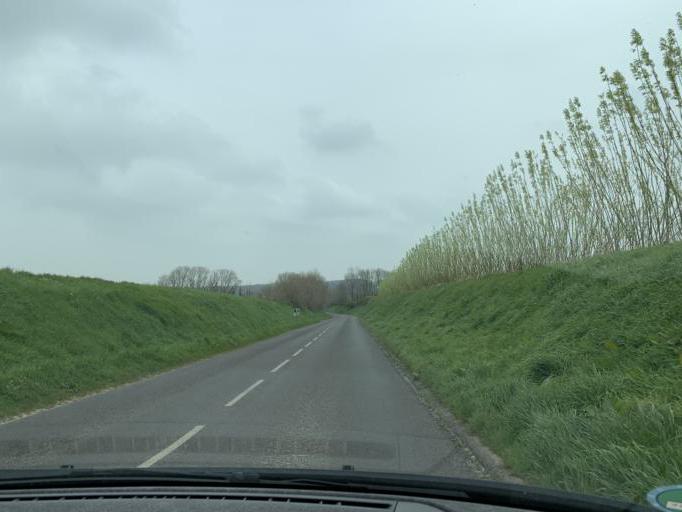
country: FR
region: Haute-Normandie
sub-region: Departement de la Seine-Maritime
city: Saint-Valery-en-Caux
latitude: 49.8548
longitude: 0.7763
